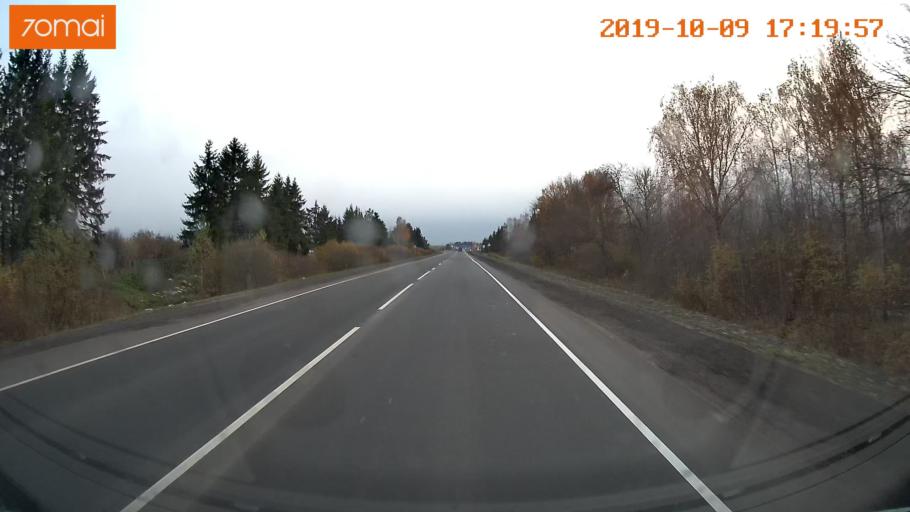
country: RU
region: Ivanovo
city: Furmanov
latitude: 57.2399
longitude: 41.1467
